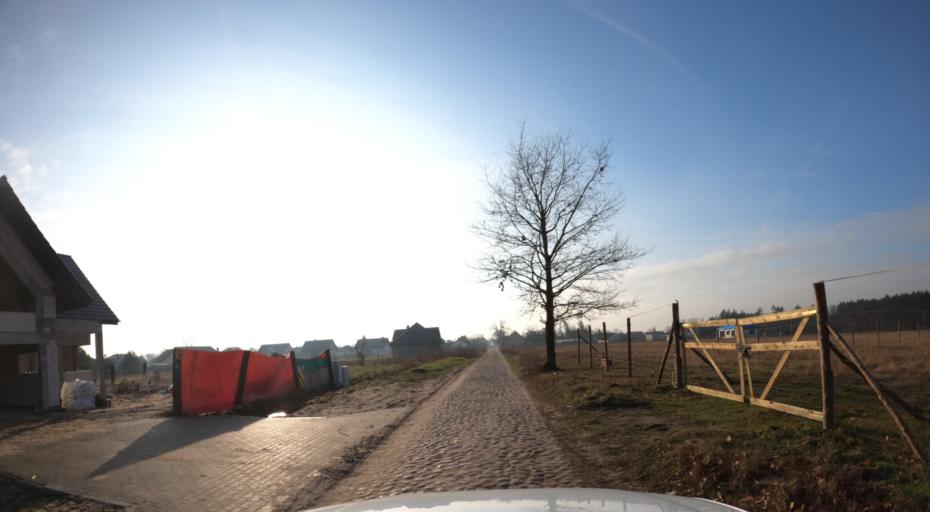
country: PL
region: Lubusz
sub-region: Powiat gorzowski
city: Kostrzyn nad Odra
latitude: 52.6183
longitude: 14.6238
